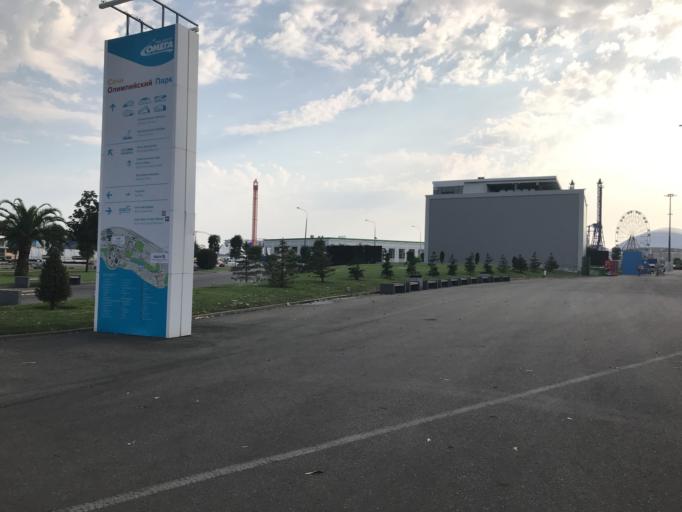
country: RU
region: Krasnodarskiy
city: Adler
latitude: 43.4080
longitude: 39.9688
